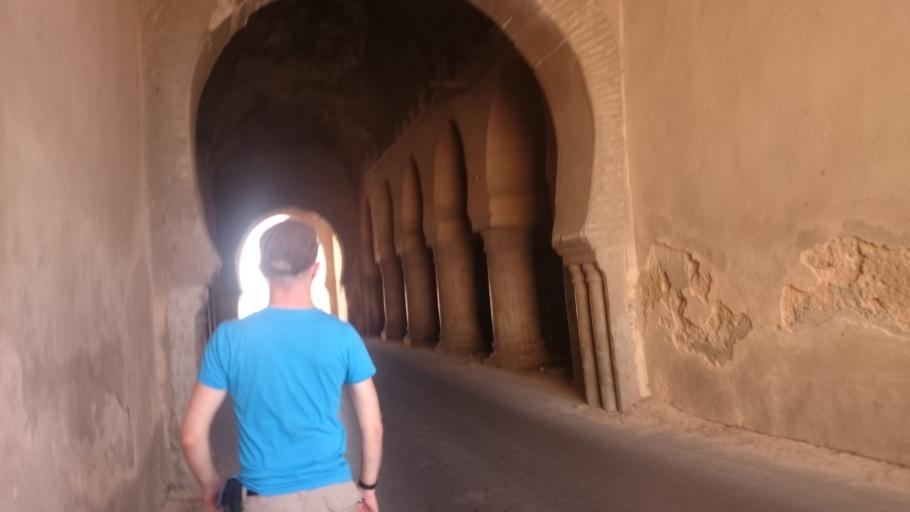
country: MA
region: Meknes-Tafilalet
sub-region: Meknes
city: Meknes
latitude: 33.8901
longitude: -5.5615
